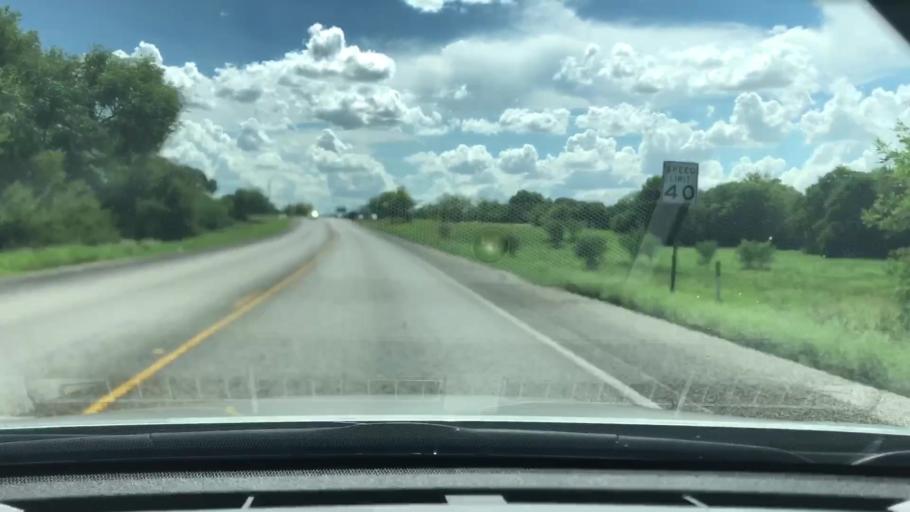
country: US
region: Texas
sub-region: Bexar County
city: Converse
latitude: 29.5230
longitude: -98.3124
